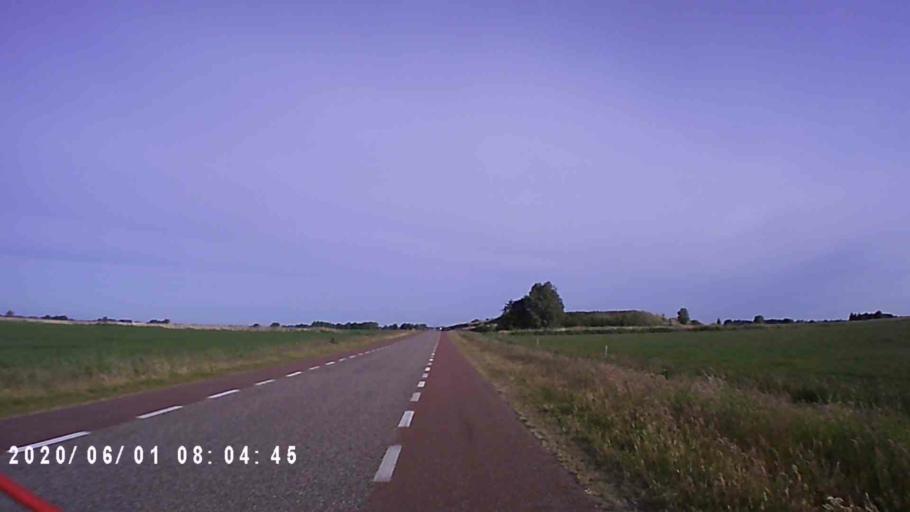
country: NL
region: Friesland
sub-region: Gemeente Tytsjerksteradiel
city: Oentsjerk
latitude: 53.2770
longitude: 5.9128
